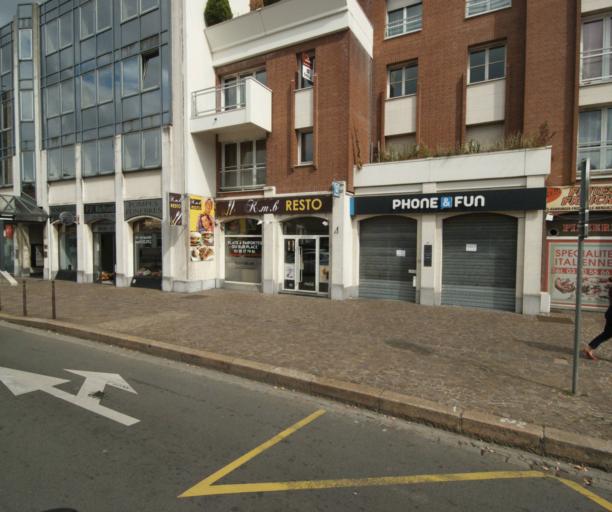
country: FR
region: Nord-Pas-de-Calais
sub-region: Departement du Nord
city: La Madeleine
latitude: 50.6549
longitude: 3.0737
